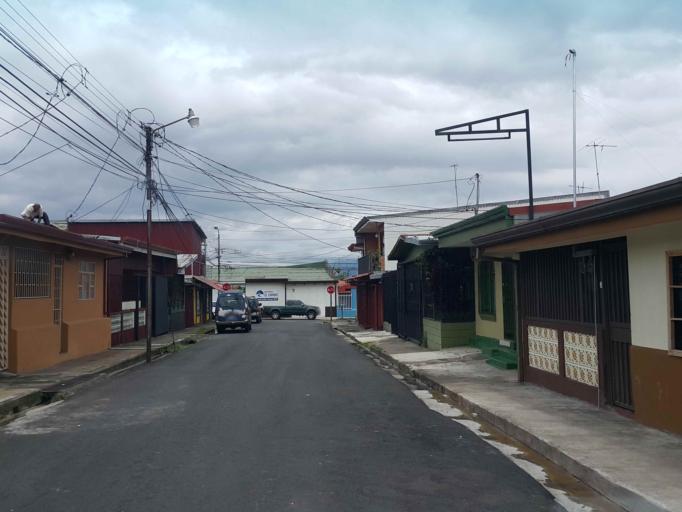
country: CR
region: Heredia
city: Mercedes
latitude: 10.0195
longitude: -84.1221
